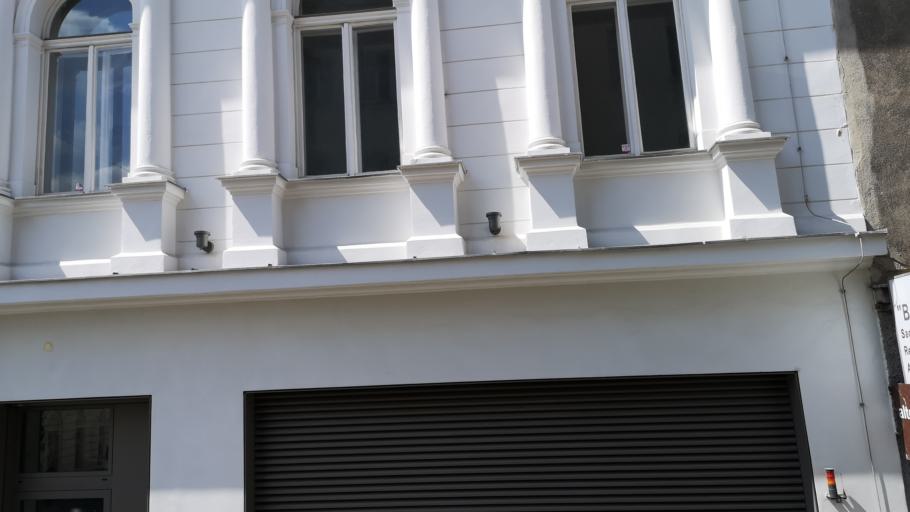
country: AT
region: Vienna
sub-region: Wien Stadt
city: Vienna
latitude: 48.1927
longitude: 16.3489
